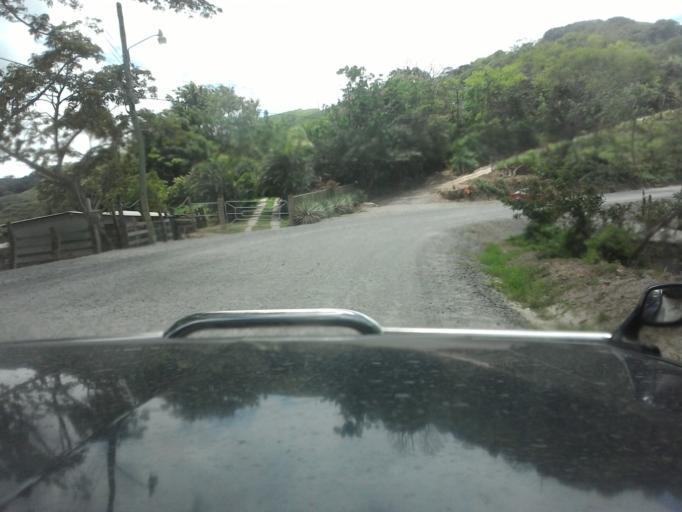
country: CR
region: Guanacaste
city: Juntas
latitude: 10.2613
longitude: -84.8420
